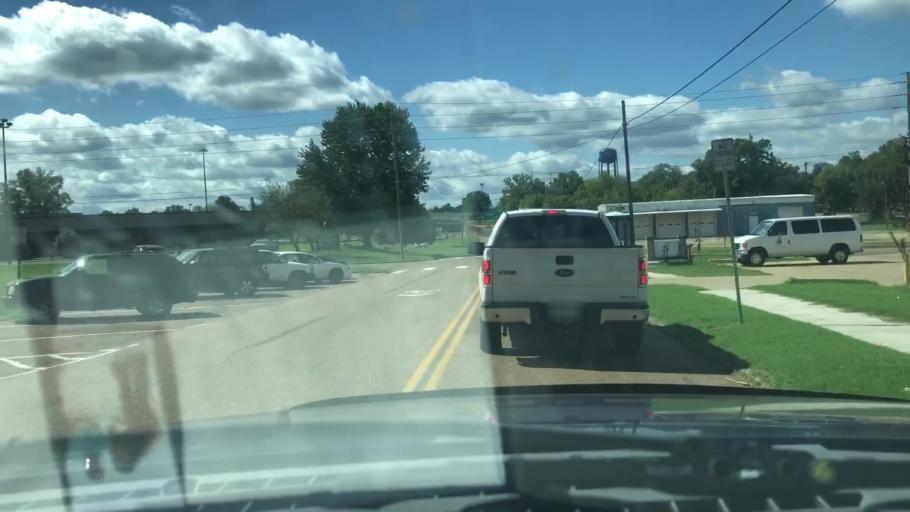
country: US
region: Texas
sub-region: Bowie County
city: Texarkana
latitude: 33.4216
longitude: -94.0480
